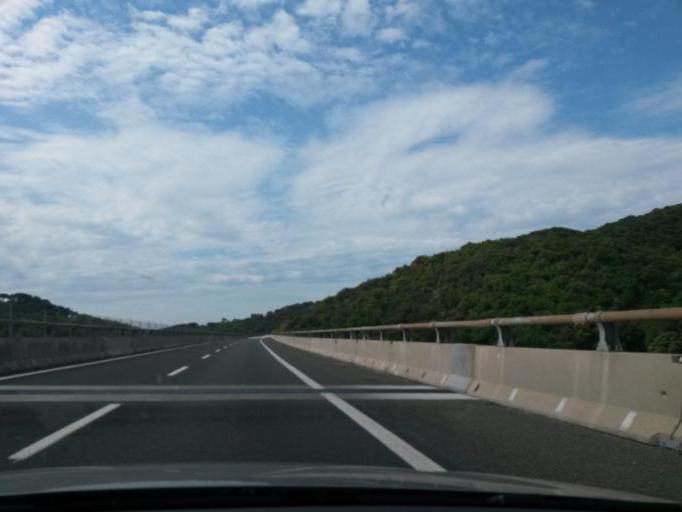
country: IT
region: Tuscany
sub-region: Provincia di Livorno
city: Rosignano Marittimo
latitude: 43.4104
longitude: 10.4923
